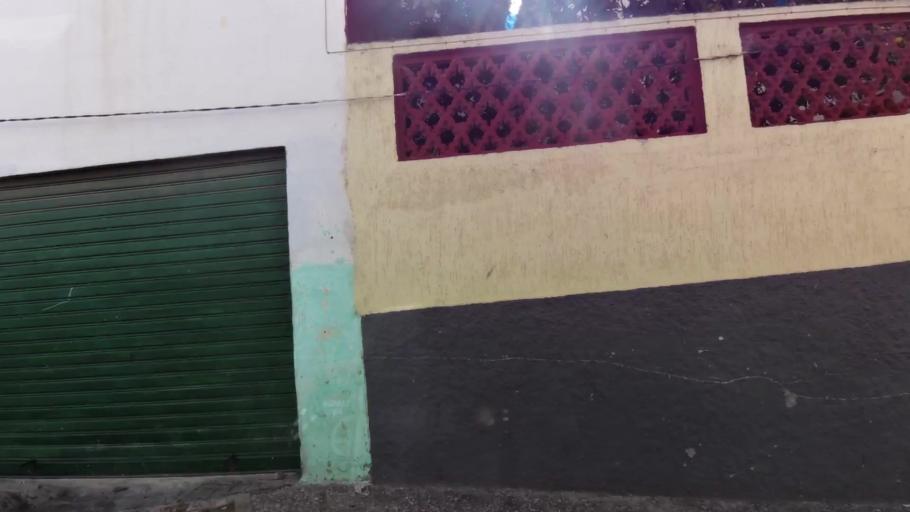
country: MA
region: Tanger-Tetouan
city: Tetouan
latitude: 35.5762
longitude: -5.3853
